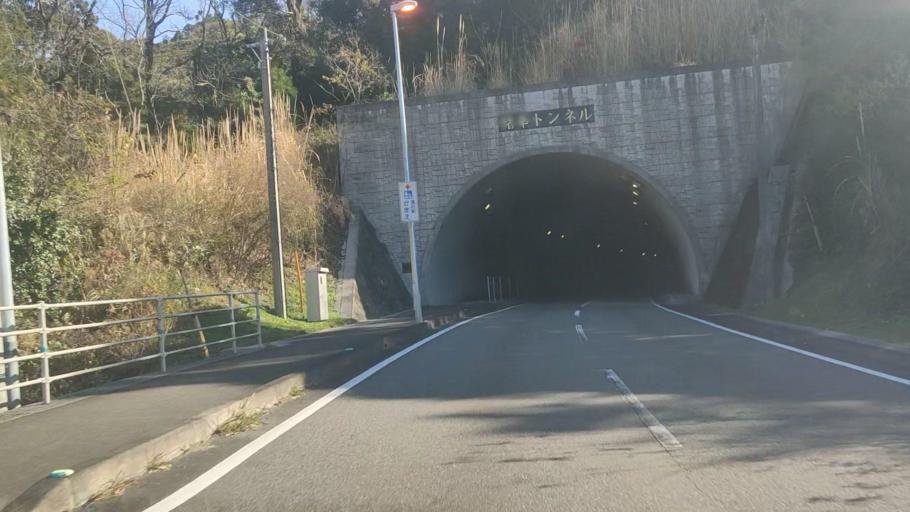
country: JP
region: Oita
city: Saiki
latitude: 32.8061
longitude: 131.8957
